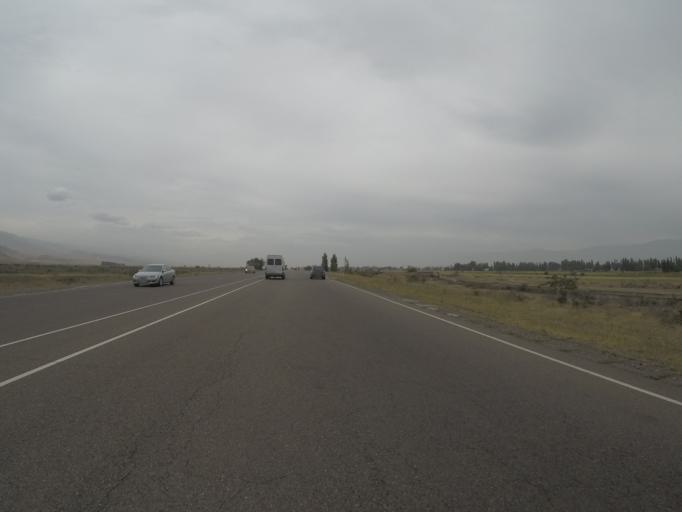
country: KG
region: Chuy
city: Bystrovka
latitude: 42.8290
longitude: 75.5297
